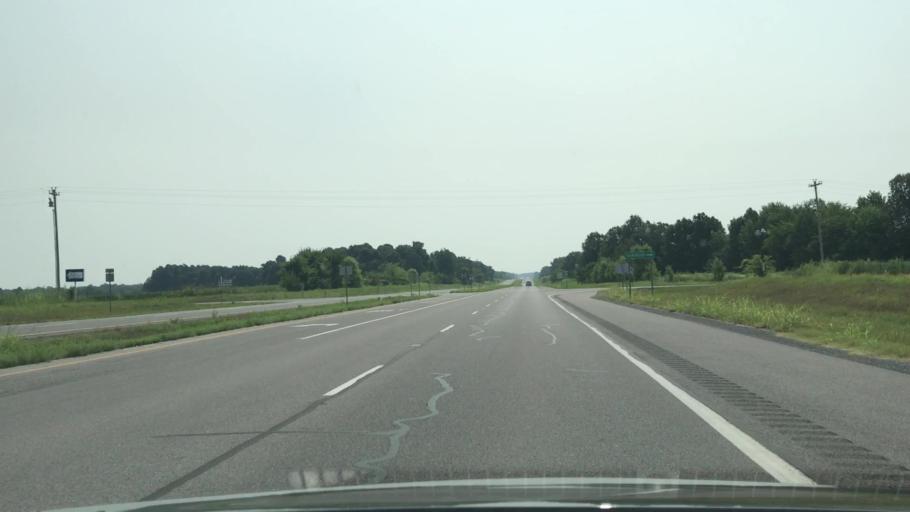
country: US
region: Kentucky
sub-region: Graves County
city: Mayfield
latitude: 36.6750
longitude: -88.5158
